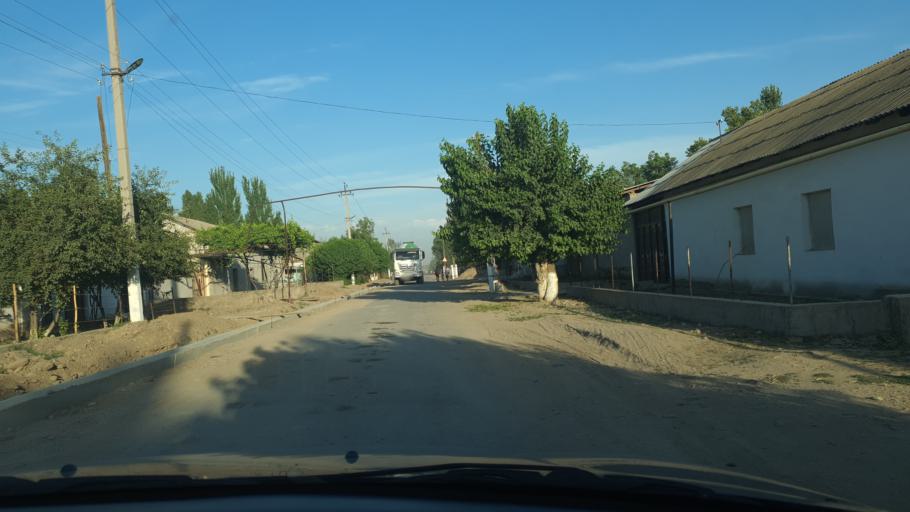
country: UZ
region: Toshkent
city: Tuytepa
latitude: 41.1051
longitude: 69.3968
